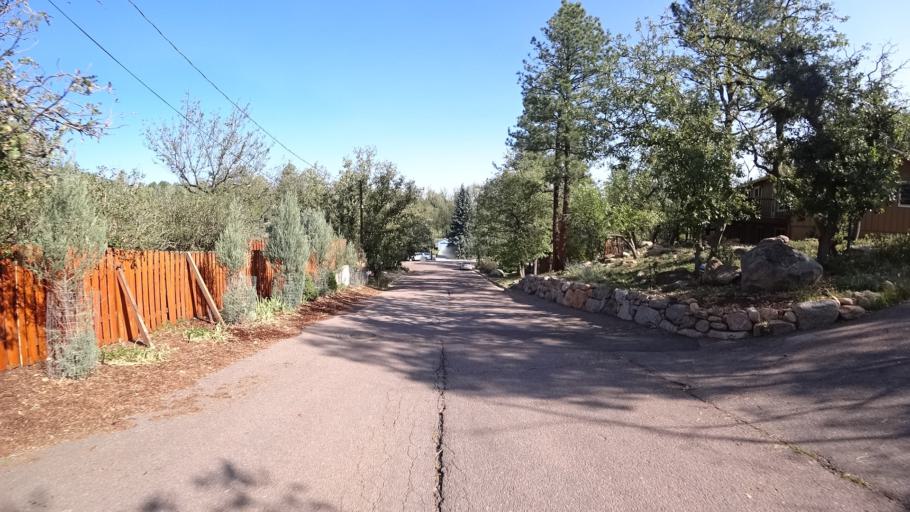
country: US
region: Colorado
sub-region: El Paso County
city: Colorado Springs
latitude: 38.7973
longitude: -104.8509
